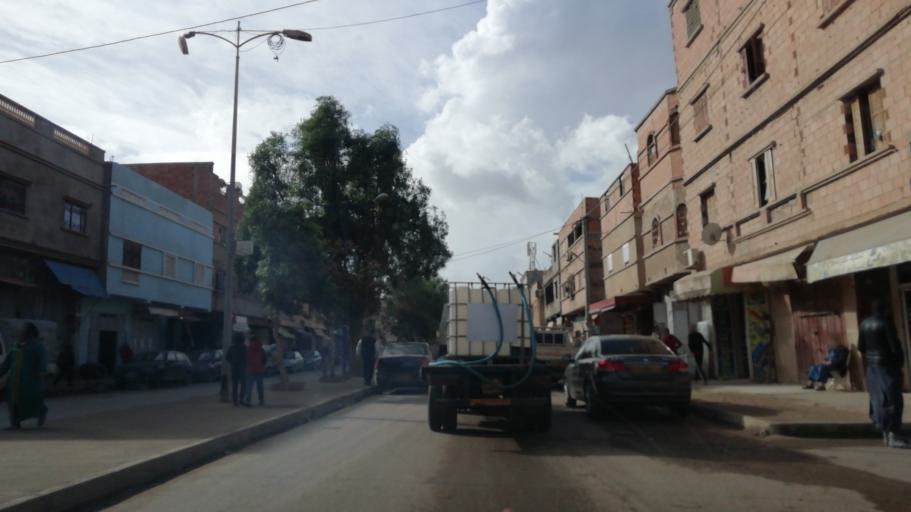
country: DZ
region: Oran
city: Es Senia
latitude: 35.6434
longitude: -0.5729
